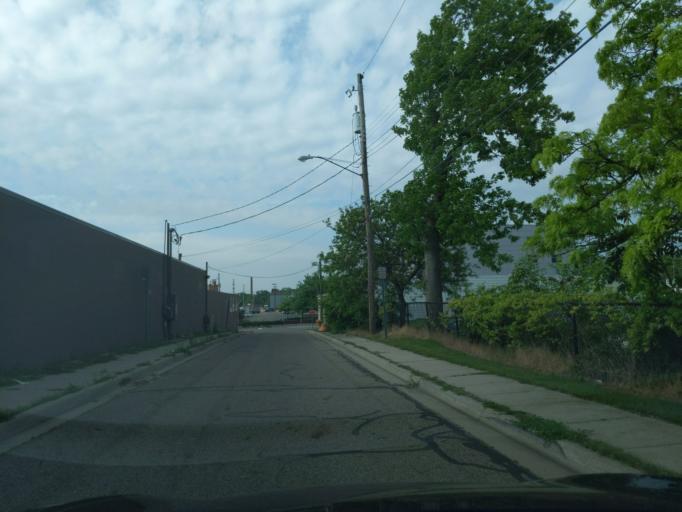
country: US
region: Michigan
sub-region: Ingham County
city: Lansing
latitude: 42.7327
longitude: -84.5419
